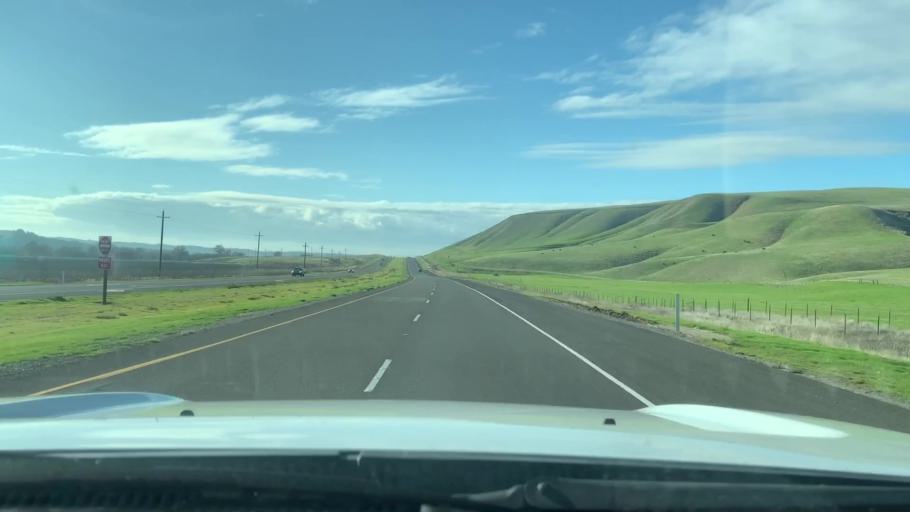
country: US
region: California
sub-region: San Luis Obispo County
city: Shandon
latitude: 35.6616
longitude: -120.4335
